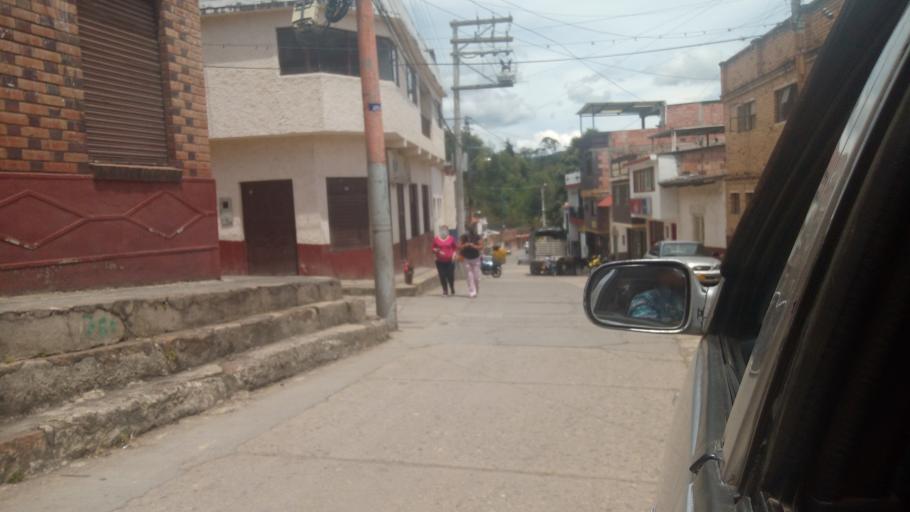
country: CO
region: Cundinamarca
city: Manta
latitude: 5.0094
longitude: -73.5408
